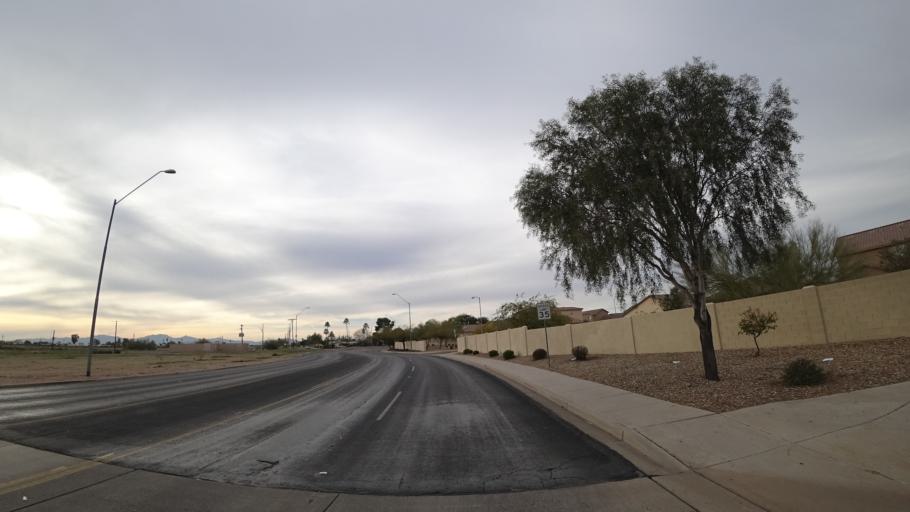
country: US
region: Arizona
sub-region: Maricopa County
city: El Mirage
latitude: 33.6233
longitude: -112.3227
